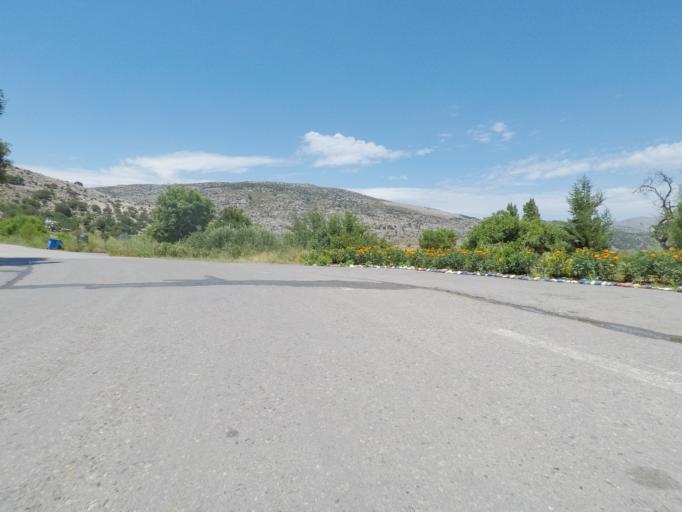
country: GR
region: Crete
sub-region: Nomos Irakleiou
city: Mokhos
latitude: 35.1856
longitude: 25.4324
